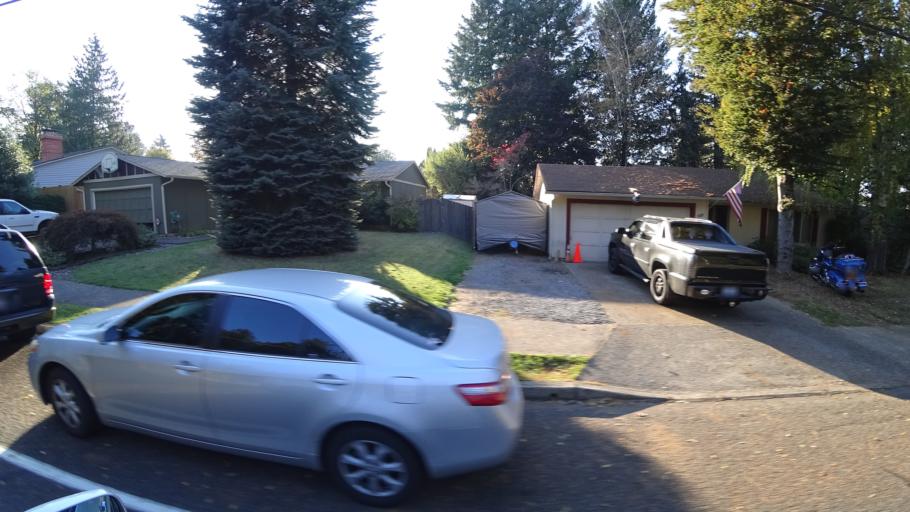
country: US
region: Oregon
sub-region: Multnomah County
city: Gresham
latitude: 45.4853
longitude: -122.4534
